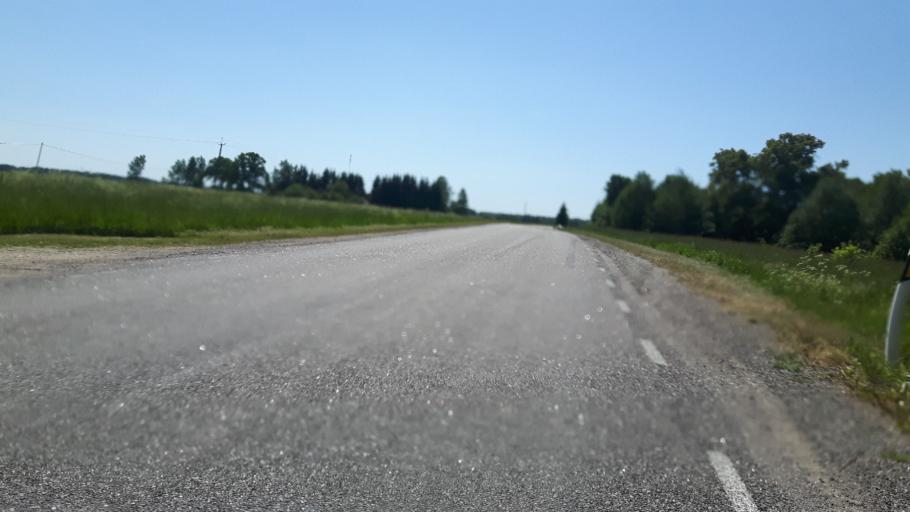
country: EE
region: Paernumaa
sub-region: Tootsi vald
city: Tootsi
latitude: 58.4902
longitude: 24.8374
